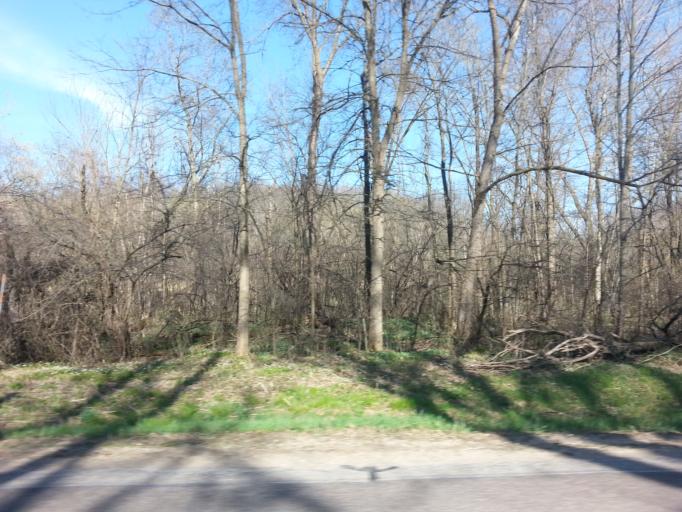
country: US
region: Wisconsin
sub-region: Pierce County
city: River Falls
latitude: 44.8181
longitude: -92.5783
